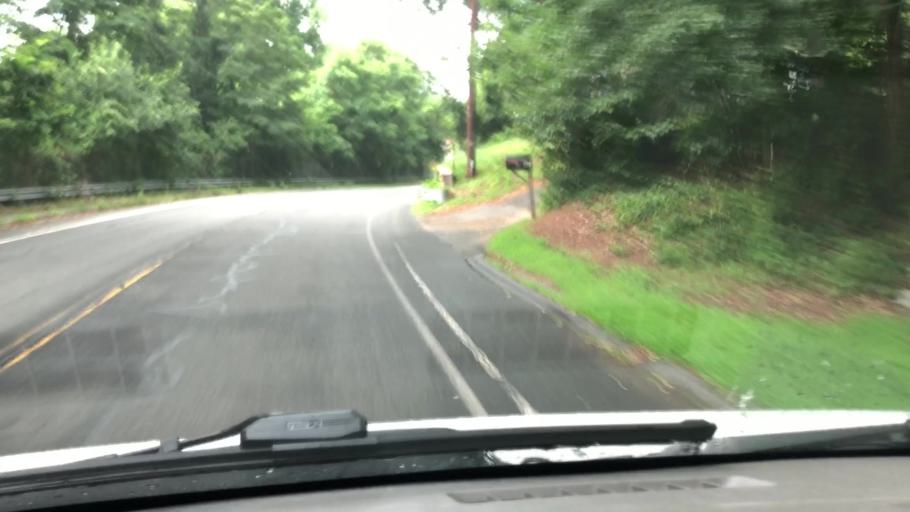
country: US
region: Massachusetts
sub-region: Hampshire County
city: Northampton
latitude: 42.3081
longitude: -72.6523
